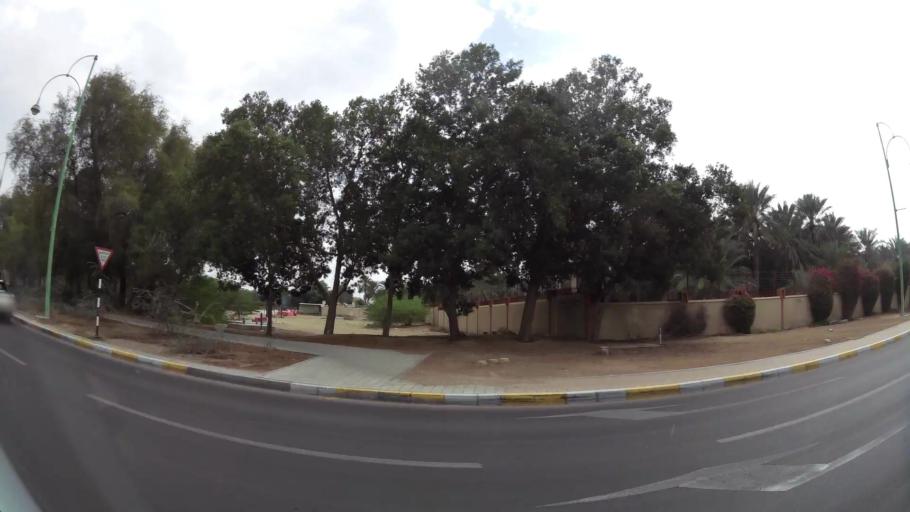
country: OM
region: Al Buraimi
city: Al Buraymi
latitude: 24.2288
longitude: 55.7697
